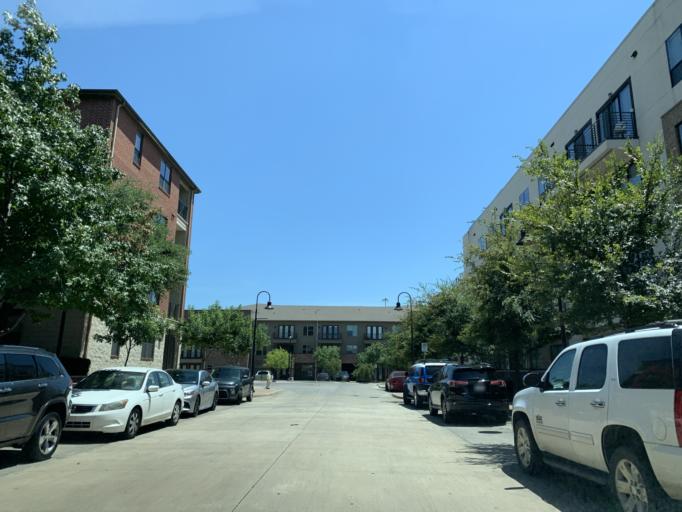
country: US
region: Texas
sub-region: Dallas County
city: Dallas
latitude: 32.7787
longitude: -96.7863
